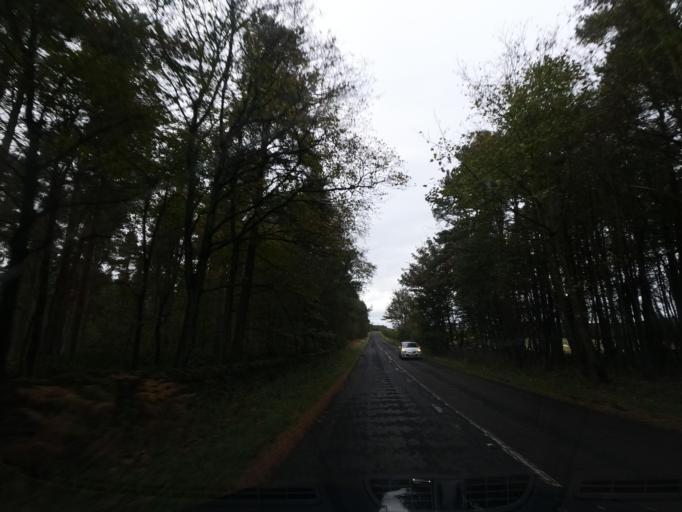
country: GB
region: England
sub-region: Northumberland
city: Doddington
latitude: 55.6030
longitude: -2.0016
